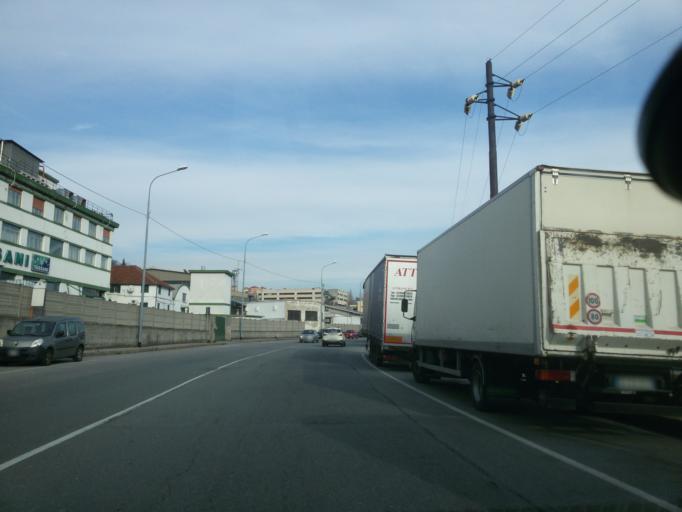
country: IT
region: Liguria
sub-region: Provincia di Genova
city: Manesseno
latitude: 44.4631
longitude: 8.8969
